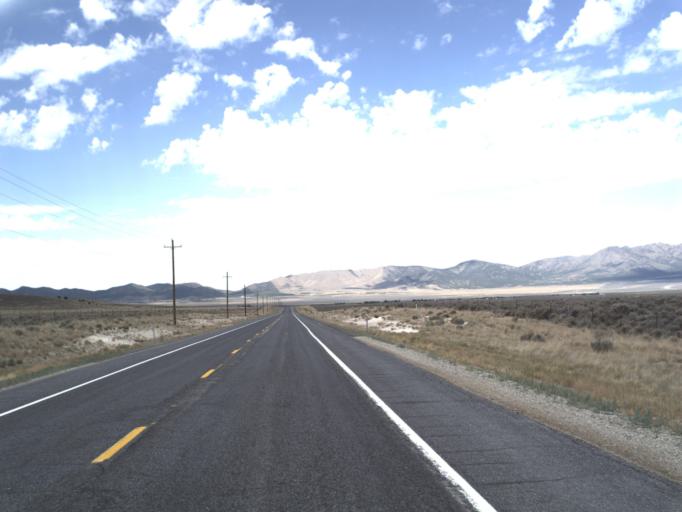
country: US
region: Utah
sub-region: Utah County
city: Eagle Mountain
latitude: 40.0744
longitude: -112.3818
